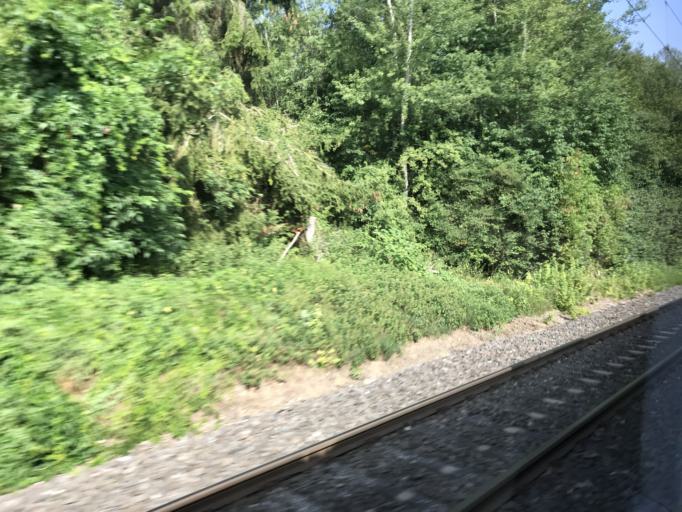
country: DE
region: Hesse
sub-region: Regierungsbezirk Giessen
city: Runkel
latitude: 50.3813
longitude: 8.1330
